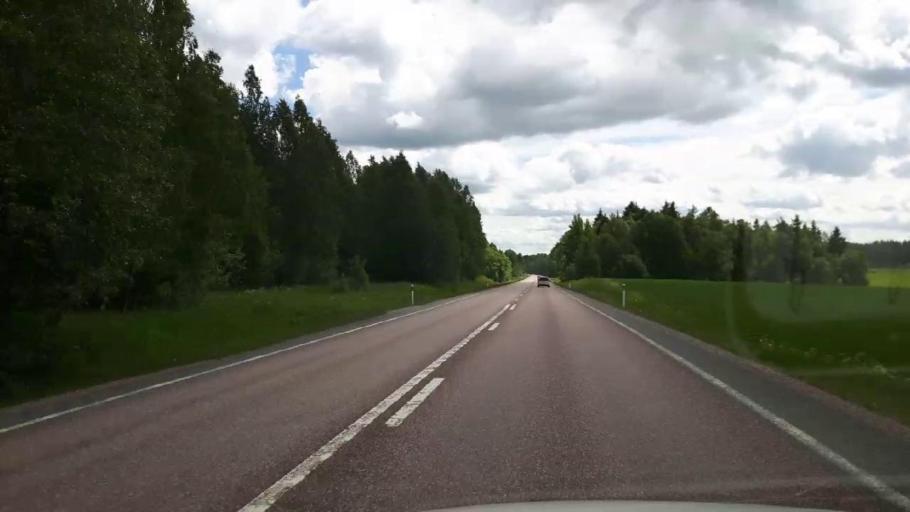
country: SE
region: Dalarna
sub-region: Saters Kommun
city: Saeter
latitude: 60.4819
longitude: 15.7740
